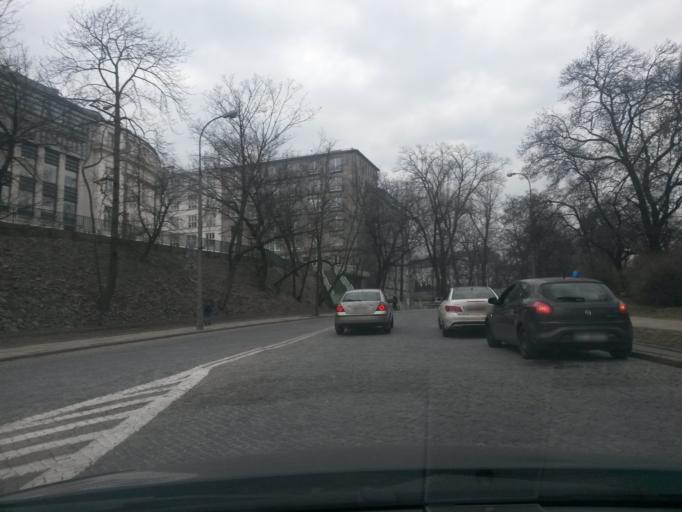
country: PL
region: Masovian Voivodeship
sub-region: Warszawa
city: Srodmiescie
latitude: 52.2424
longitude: 21.0192
